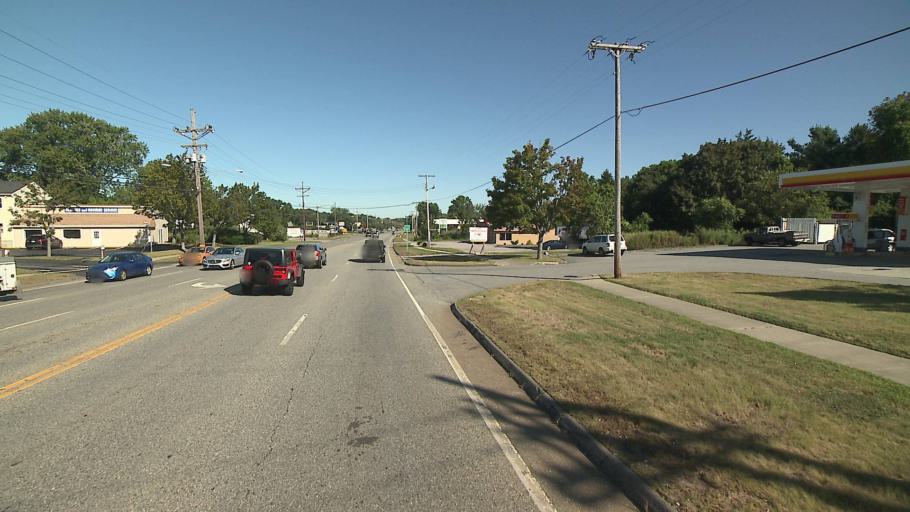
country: US
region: Connecticut
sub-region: New London County
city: Conning Towers-Nautilus Park
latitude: 41.3701
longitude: -72.0711
